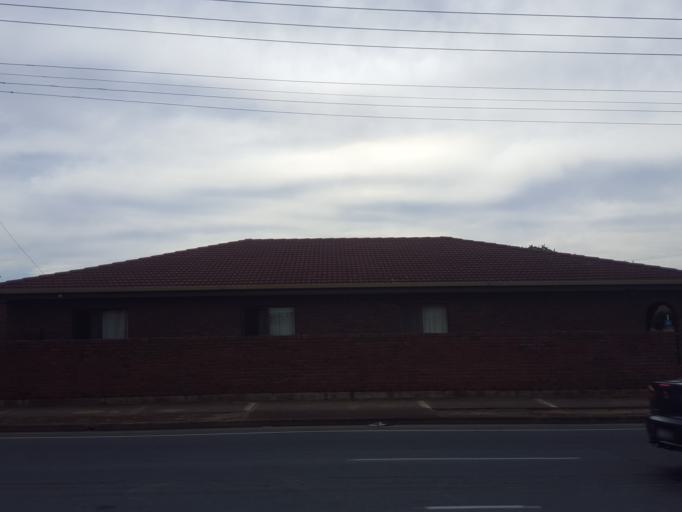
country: AU
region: South Australia
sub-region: Charles Sturt
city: Woodville North
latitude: -34.8626
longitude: 138.5476
